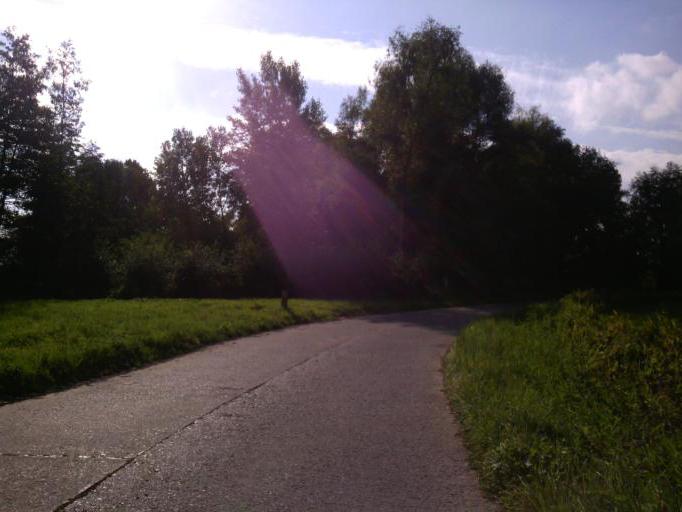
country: BE
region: Wallonia
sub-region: Province du Hainaut
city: Flobecq
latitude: 50.6859
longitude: 3.7551
